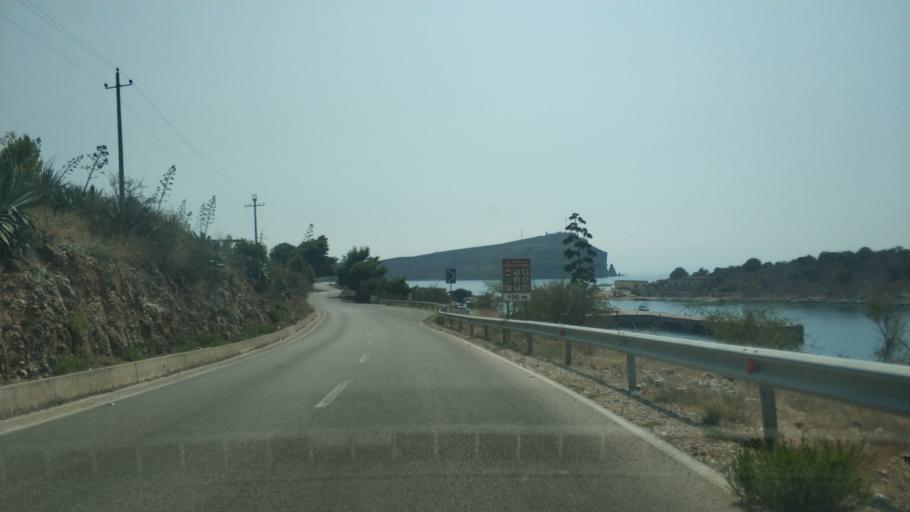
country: AL
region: Vlore
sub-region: Rrethi i Vlores
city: Himare
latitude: 40.0654
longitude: 19.7932
